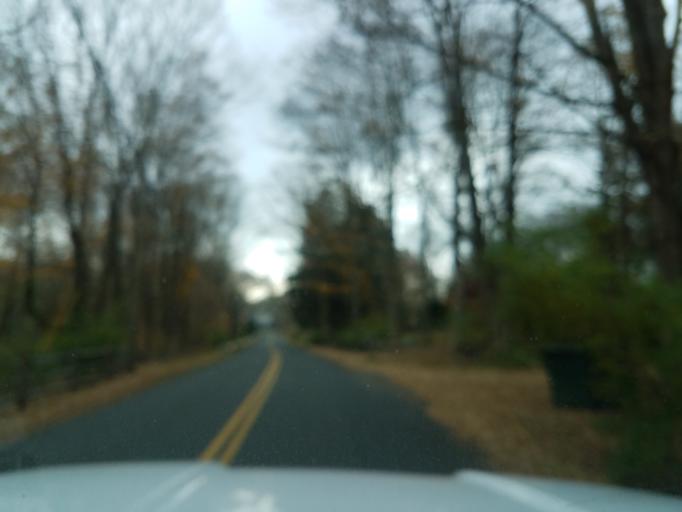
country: US
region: Connecticut
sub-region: New Haven County
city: Middlebury
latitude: 41.5077
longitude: -73.1604
